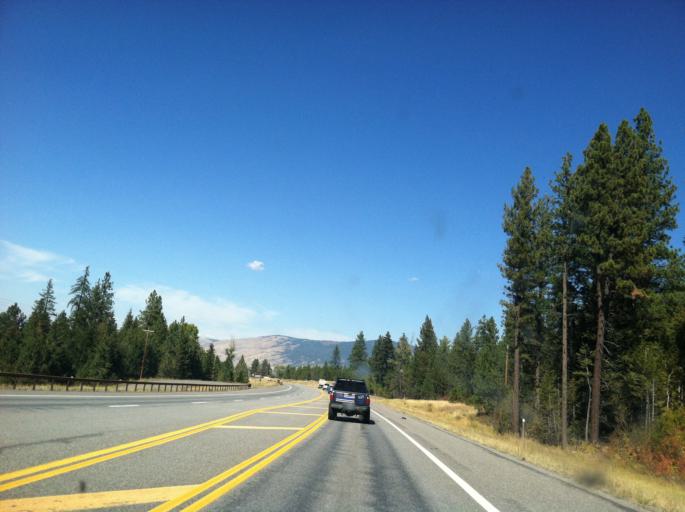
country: US
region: Montana
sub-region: Missoula County
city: Frenchtown
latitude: 47.0904
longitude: -114.0405
